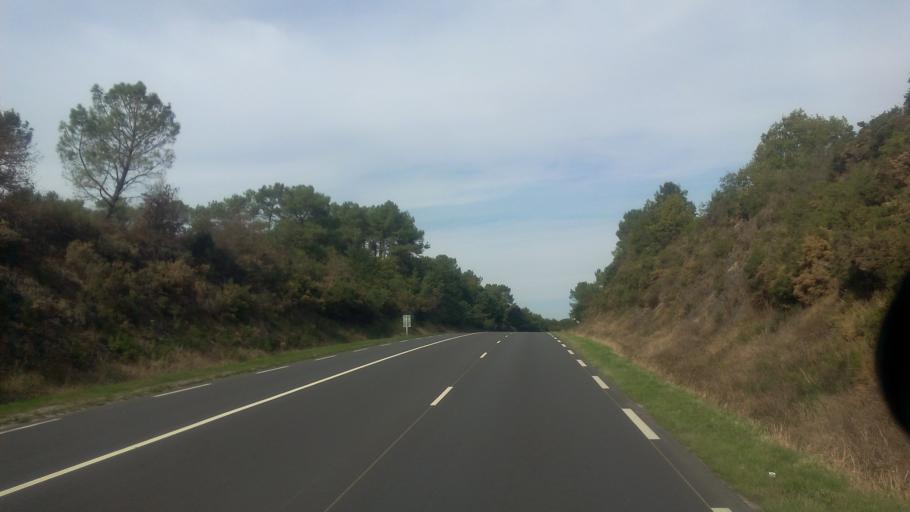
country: FR
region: Brittany
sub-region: Departement du Morbihan
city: Saint-Perreux
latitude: 47.6808
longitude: -2.0851
